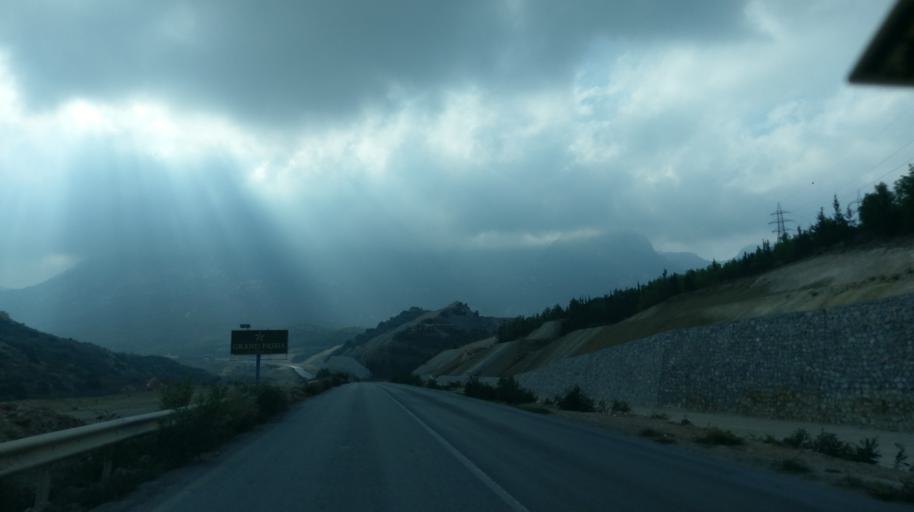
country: CY
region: Keryneia
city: Kyrenia
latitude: 35.3136
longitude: 33.4232
